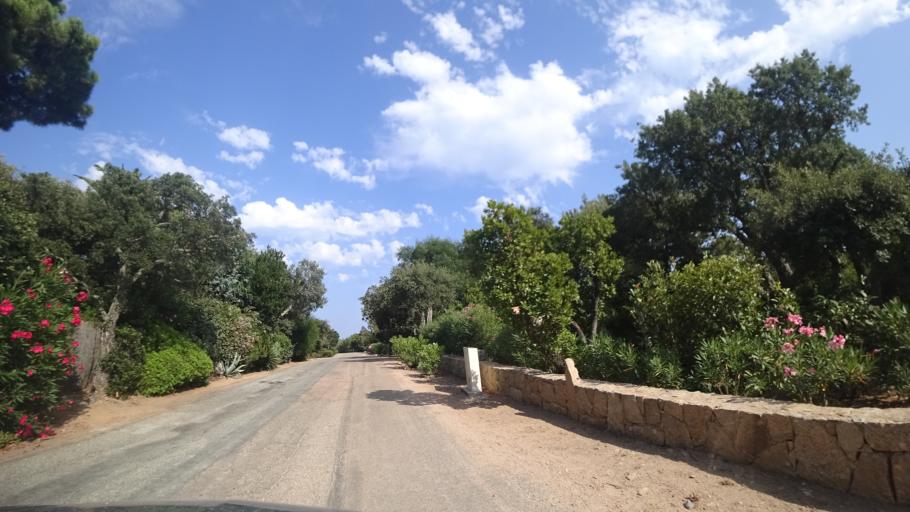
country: FR
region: Corsica
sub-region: Departement de la Corse-du-Sud
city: Porto-Vecchio
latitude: 41.6200
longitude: 9.3465
